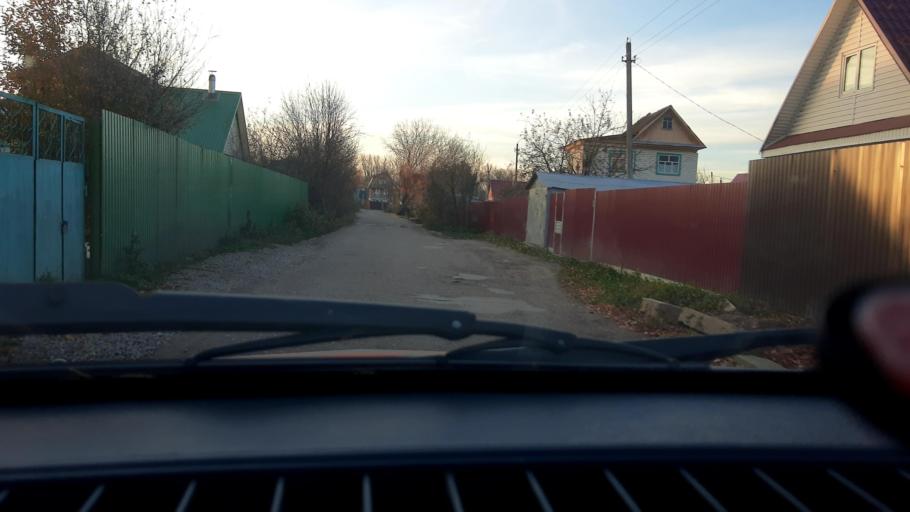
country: RU
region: Bashkortostan
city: Ufa
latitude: 54.6900
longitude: 55.9017
